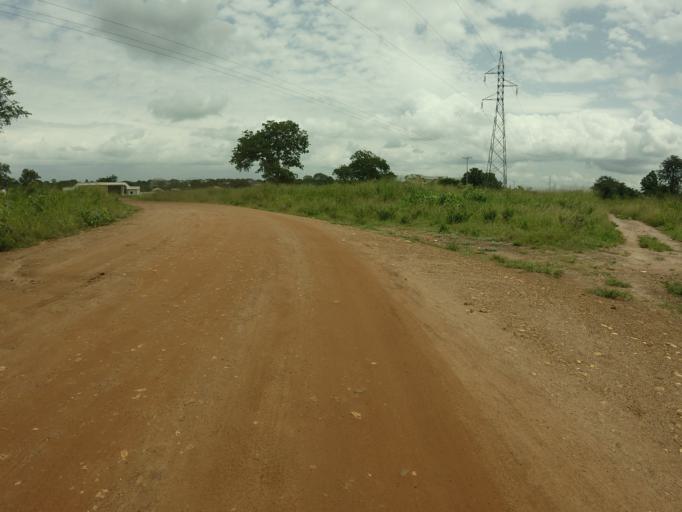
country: GH
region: Volta
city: Ho
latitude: 6.5875
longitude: 0.4670
